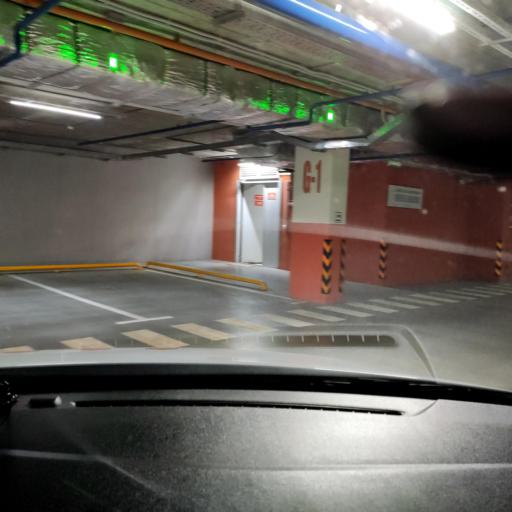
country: RU
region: Tatarstan
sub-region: Gorod Kazan'
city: Kazan
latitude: 55.8009
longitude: 49.1286
